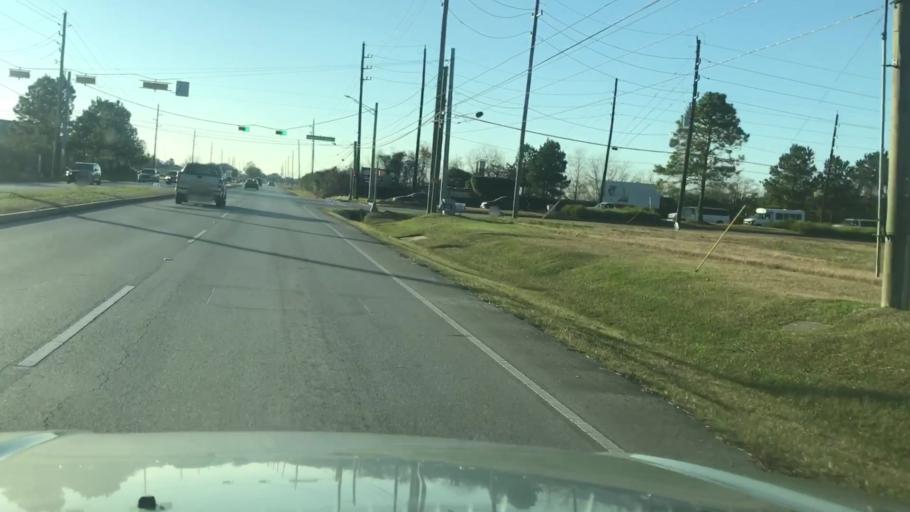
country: US
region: Texas
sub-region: Fort Bend County
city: Cinco Ranch
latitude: 29.8313
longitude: -95.7289
